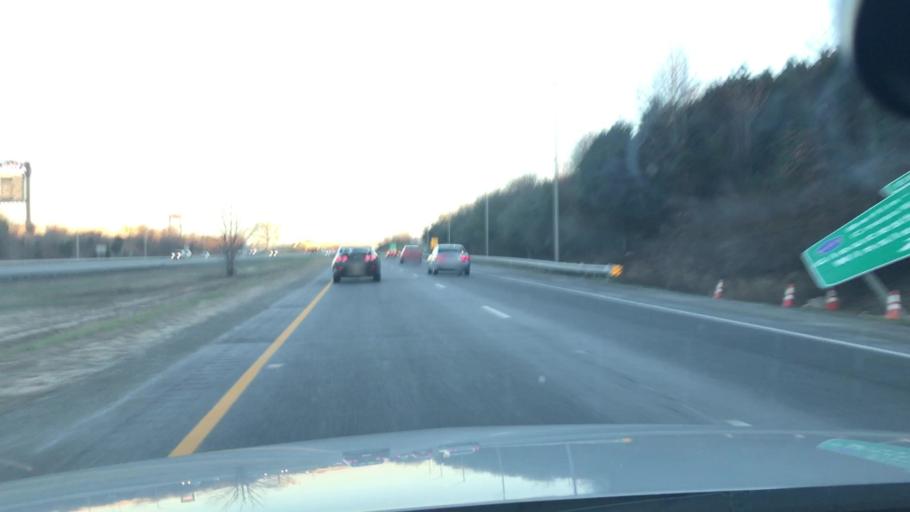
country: US
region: New Jersey
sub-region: Camden County
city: Sicklerville
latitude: 39.7371
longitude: -75.0126
